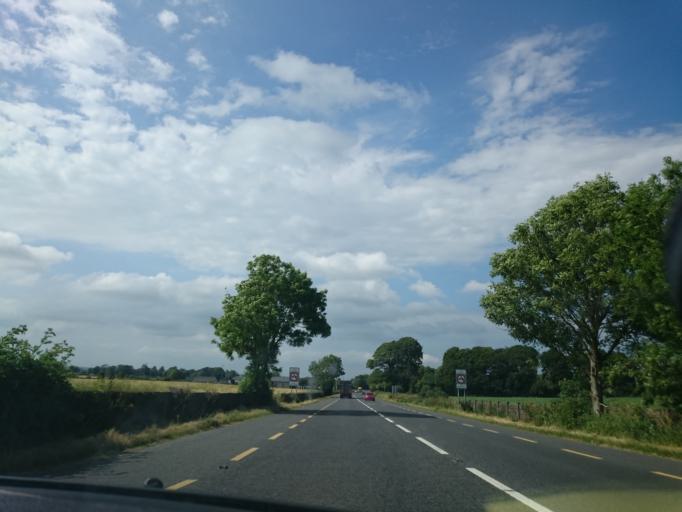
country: IE
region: Leinster
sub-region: Kilkenny
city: Kilkenny
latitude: 52.6188
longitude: -7.2483
